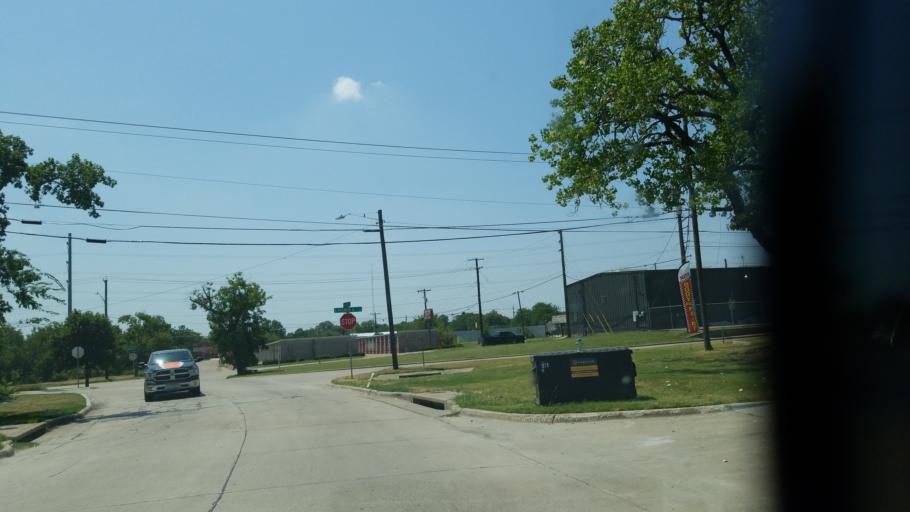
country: US
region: Texas
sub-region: Dallas County
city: Garland
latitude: 32.9115
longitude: -96.6284
